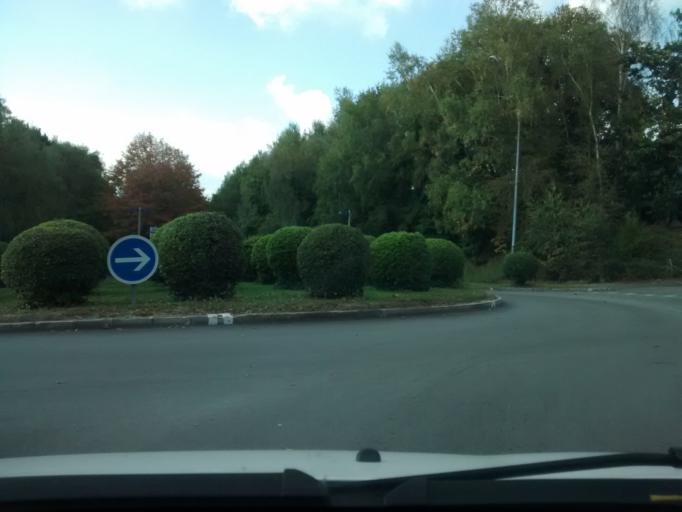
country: FR
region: Pays de la Loire
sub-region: Departement de la Loire-Atlantique
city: Orvault
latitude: 47.2625
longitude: -1.5938
